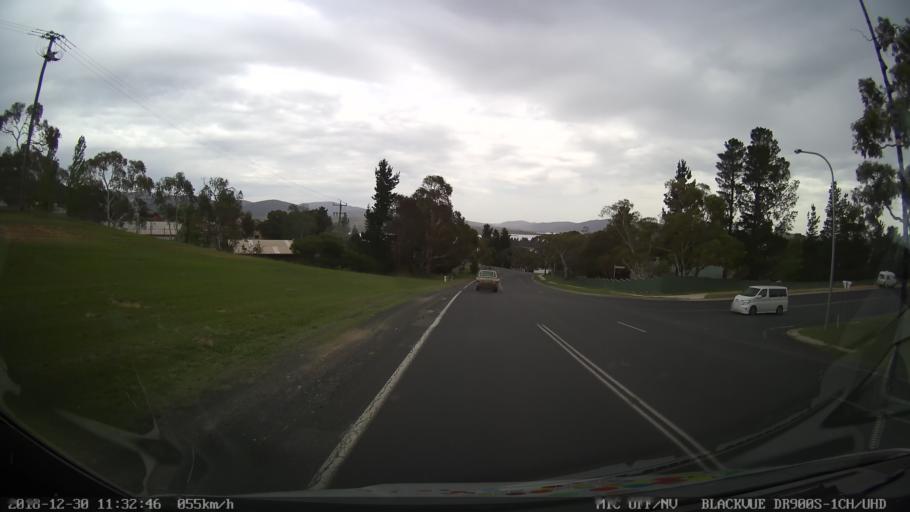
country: AU
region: New South Wales
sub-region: Snowy River
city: Jindabyne
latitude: -36.4194
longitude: 148.6104
